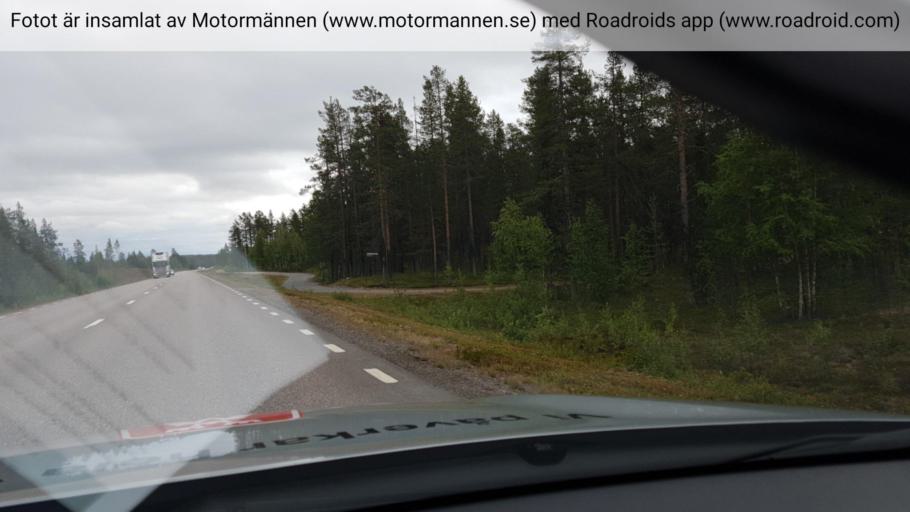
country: SE
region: Norrbotten
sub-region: Gallivare Kommun
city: Gaellivare
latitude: 67.0772
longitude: 21.0788
